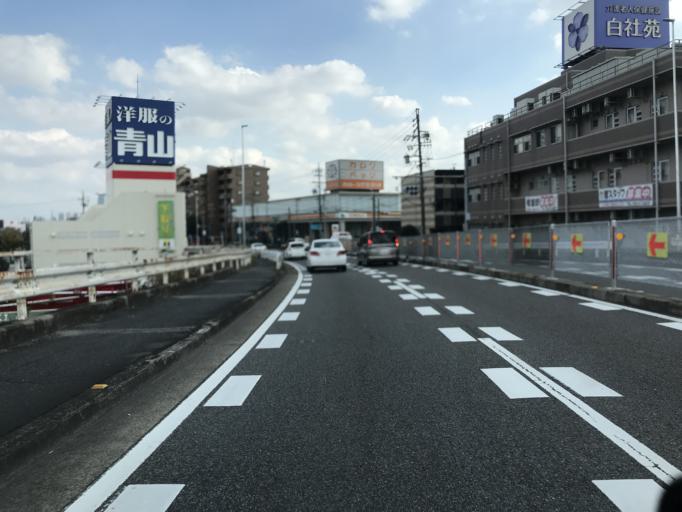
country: JP
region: Aichi
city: Nagoya-shi
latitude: 35.1780
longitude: 136.8483
